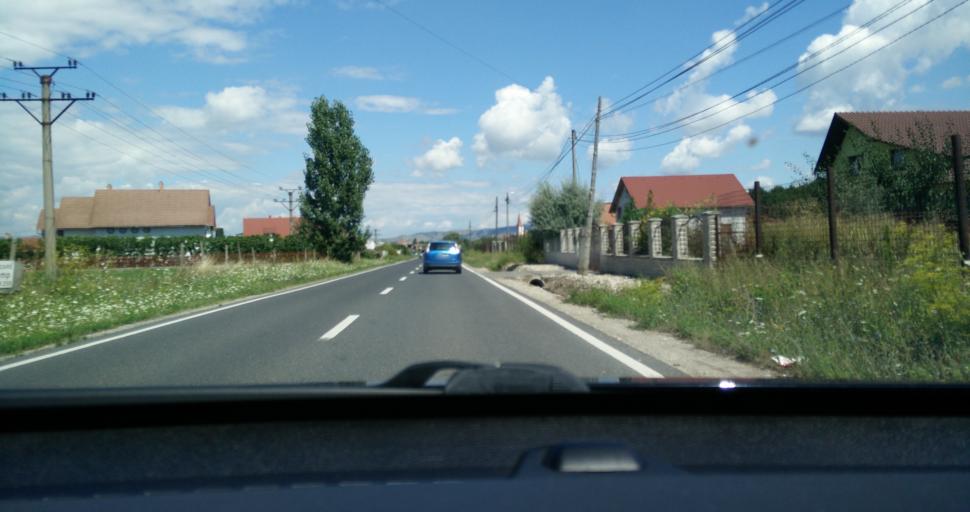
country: RO
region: Alba
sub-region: Municipiul Sebes
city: Petresti
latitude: 45.9134
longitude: 23.5546
